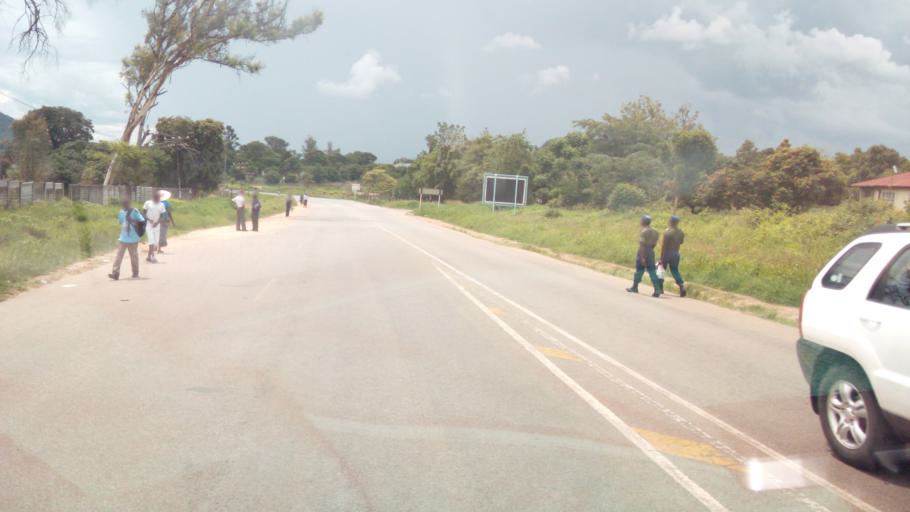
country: ZW
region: Mashonaland Central
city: Bindura
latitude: -17.3040
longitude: 31.3266
